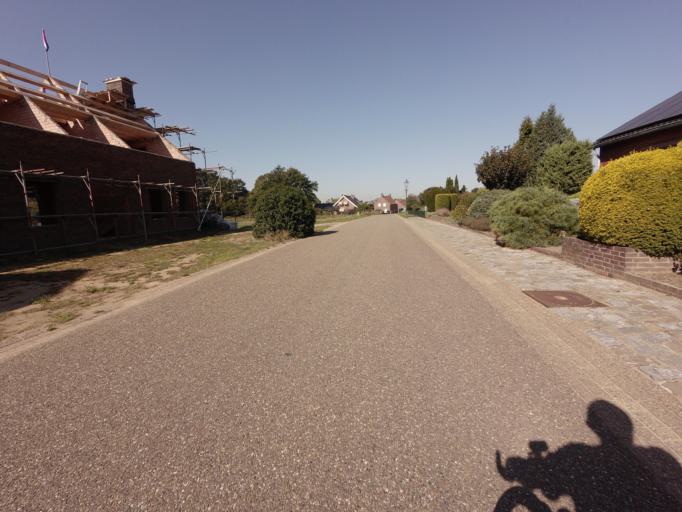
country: NL
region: Limburg
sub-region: Gemeente Roerdalen
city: Melick
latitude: 51.1559
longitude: 6.0359
